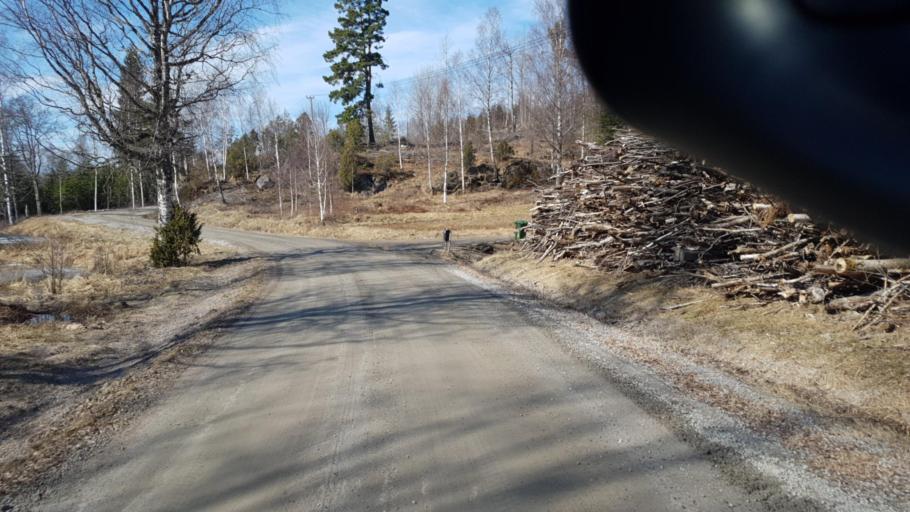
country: SE
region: Vaermland
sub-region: Arvika Kommun
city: Arvika
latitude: 59.7115
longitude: 12.8513
